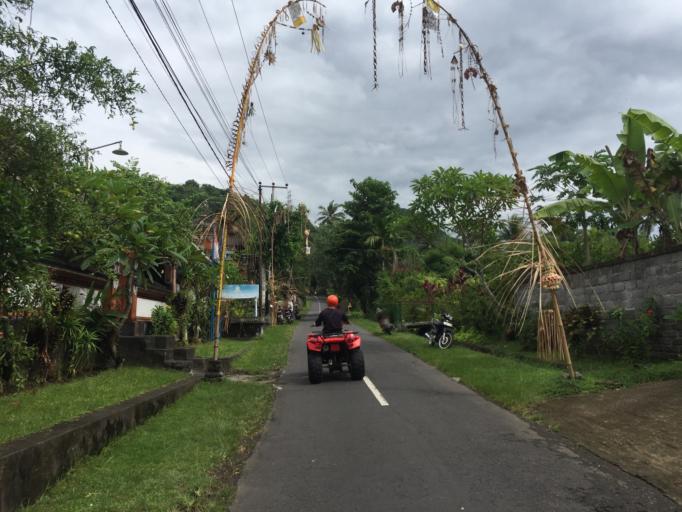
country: ID
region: Bali
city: Banjar Kawan
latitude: -8.4850
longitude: 115.5243
